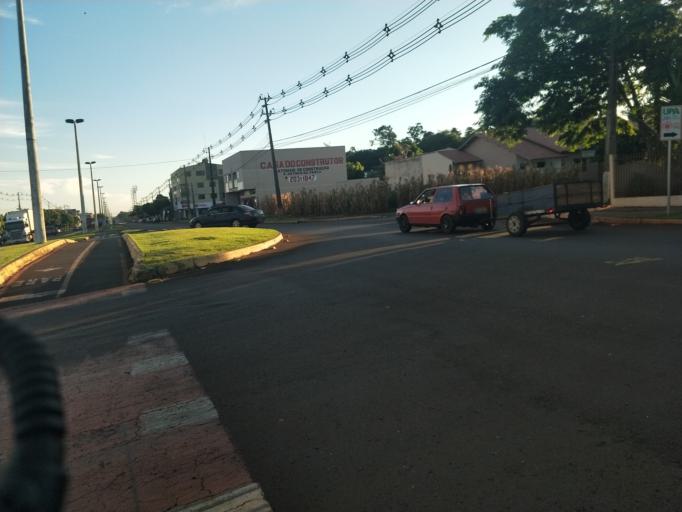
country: BR
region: Parana
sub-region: Marechal Candido Rondon
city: Marechal Candido Rondon
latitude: -24.5496
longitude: -54.0454
